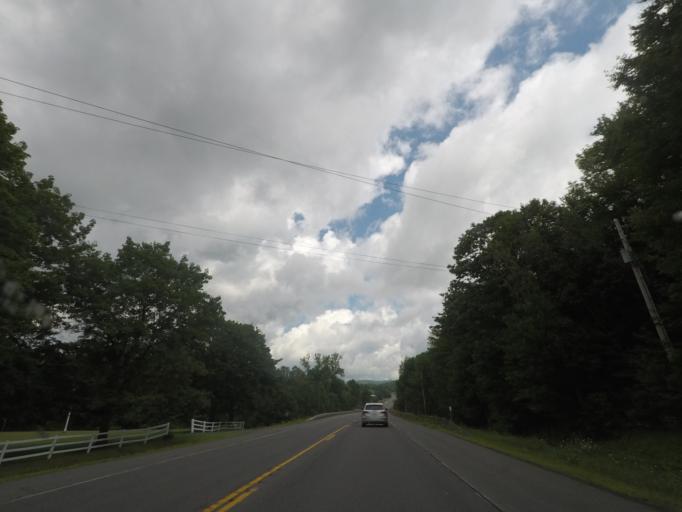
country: US
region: Massachusetts
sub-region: Berkshire County
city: Lanesborough
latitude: 42.5890
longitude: -73.3679
